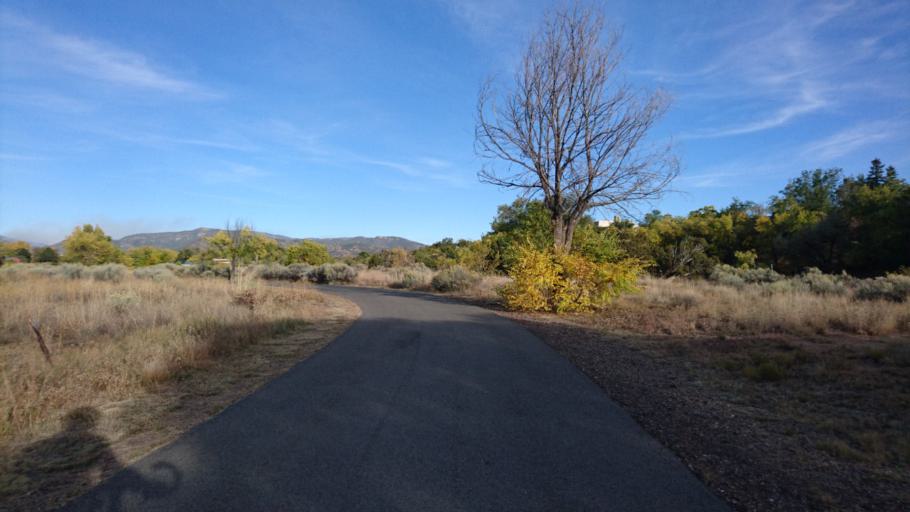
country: US
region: New Mexico
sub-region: Santa Fe County
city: Agua Fria
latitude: 35.6447
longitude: -105.9773
